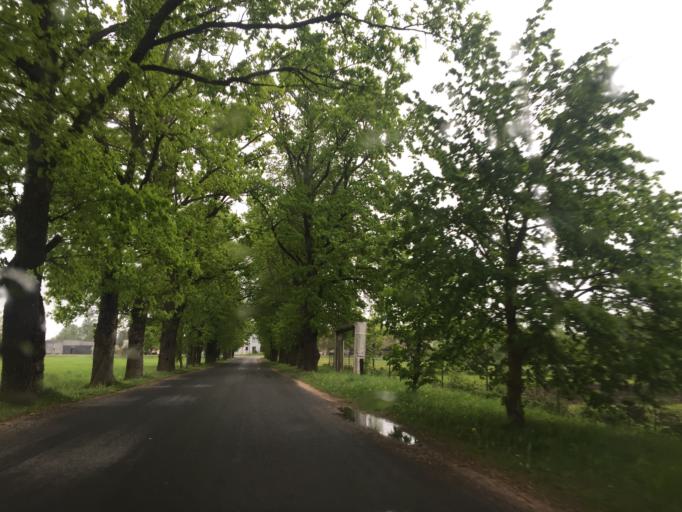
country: LV
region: Lielvarde
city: Lielvarde
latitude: 56.7142
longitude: 24.8320
